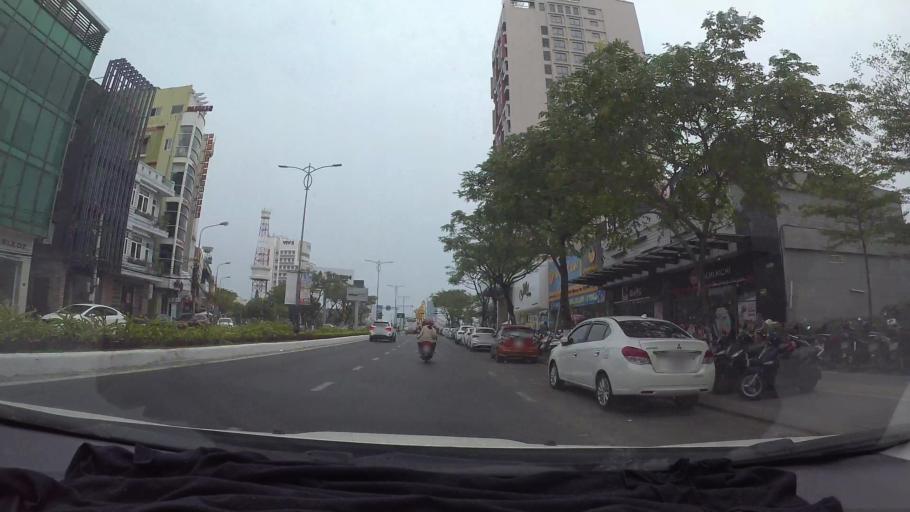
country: VN
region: Da Nang
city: Da Nang
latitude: 16.0609
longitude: 108.2218
